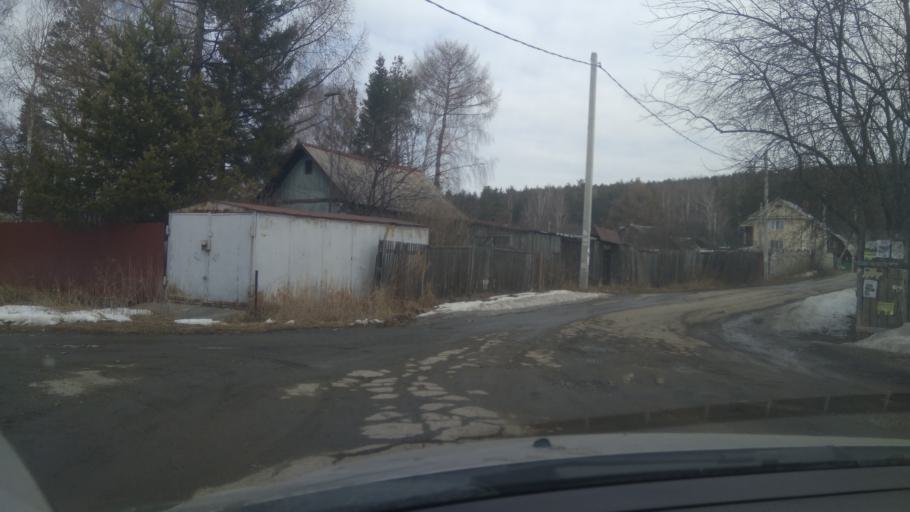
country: RU
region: Sverdlovsk
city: Severka
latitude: 56.8521
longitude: 60.3831
